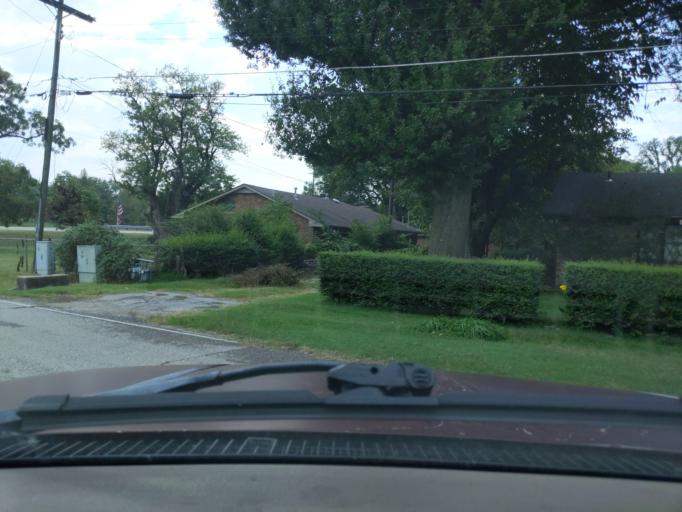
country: US
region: Oklahoma
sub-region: Rogers County
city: Catoosa
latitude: 36.1485
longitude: -95.8232
